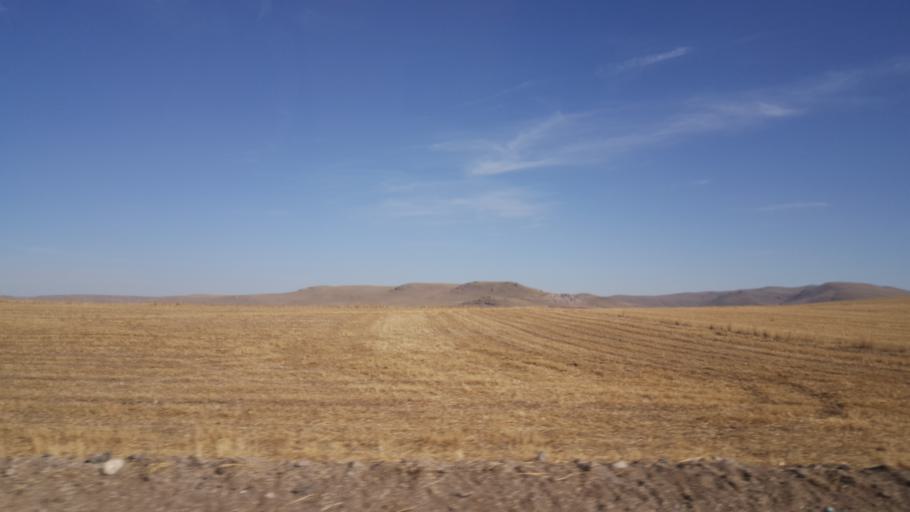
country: TR
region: Ankara
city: Yenice
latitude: 39.3261
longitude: 32.7550
